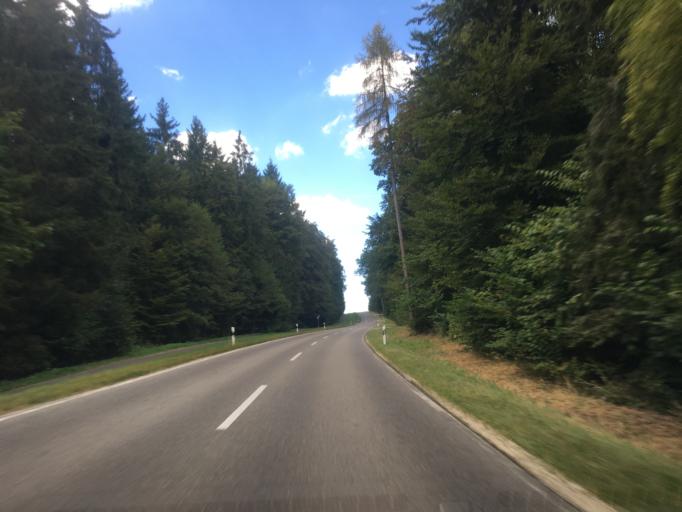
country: DE
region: Baden-Wuerttemberg
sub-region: Tuebingen Region
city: Hayingen
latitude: 48.3008
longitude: 9.4515
